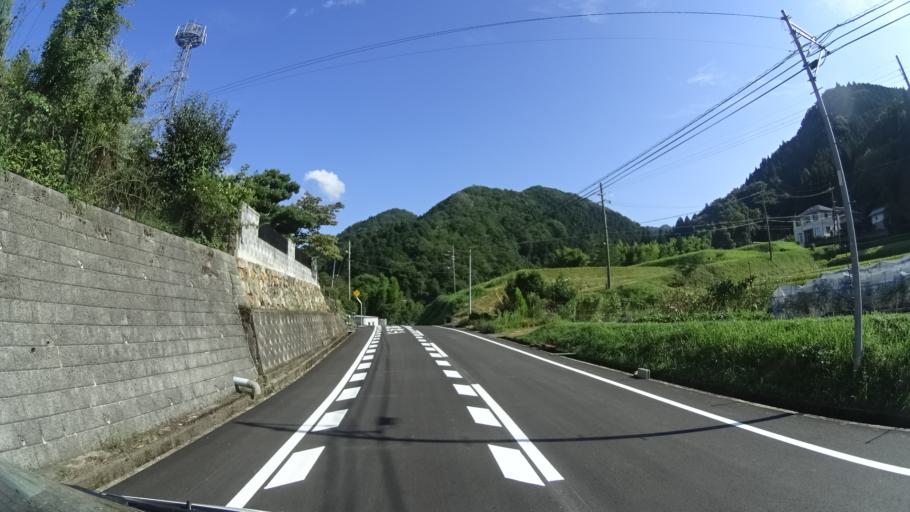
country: JP
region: Kyoto
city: Ayabe
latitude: 35.2708
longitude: 135.3613
